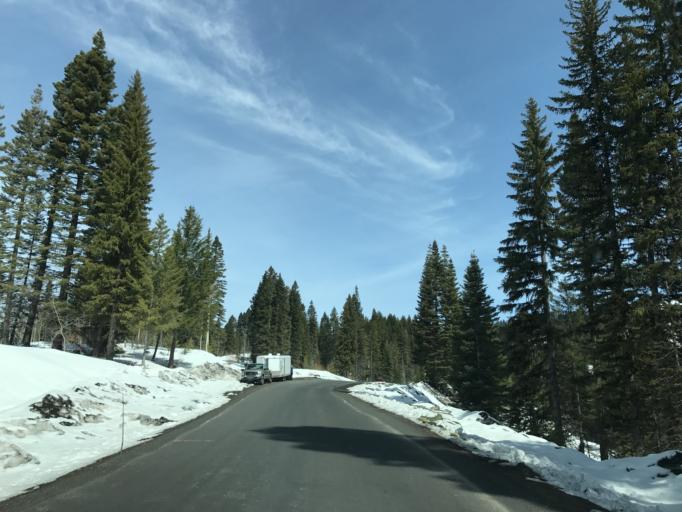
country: US
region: Idaho
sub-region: Valley County
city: McCall
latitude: 45.0007
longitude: -116.1620
